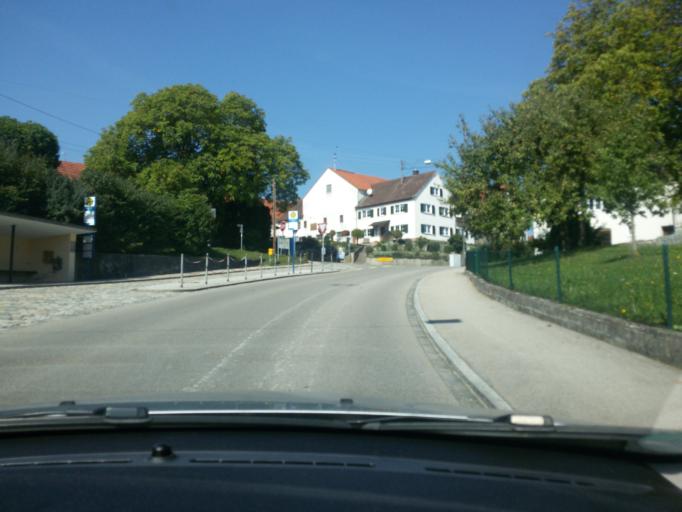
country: DE
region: Bavaria
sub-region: Swabia
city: Munster
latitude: 48.2066
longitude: 10.6483
